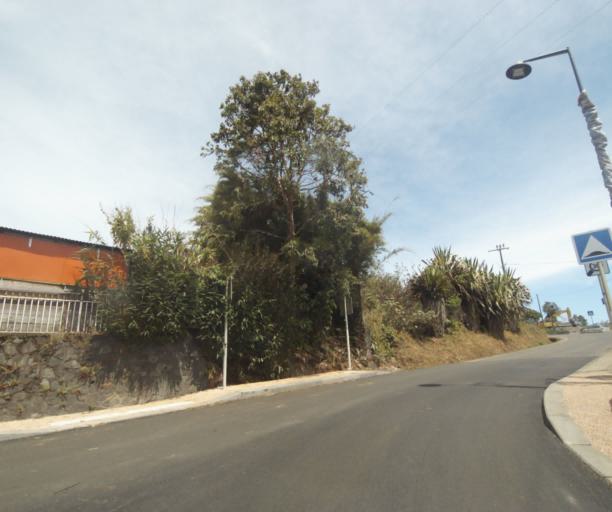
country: RE
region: Reunion
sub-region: Reunion
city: Saint-Paul
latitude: -21.0399
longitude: 55.3046
